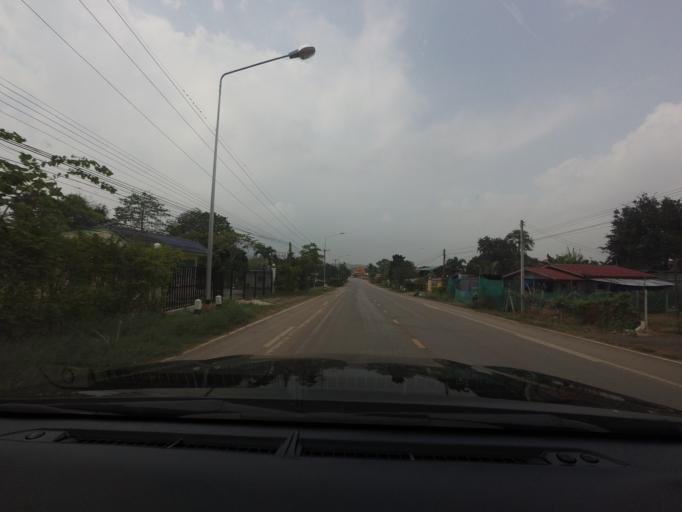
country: TH
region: Nakhon Ratchasima
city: Pak Chong
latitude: 14.4755
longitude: 101.5675
